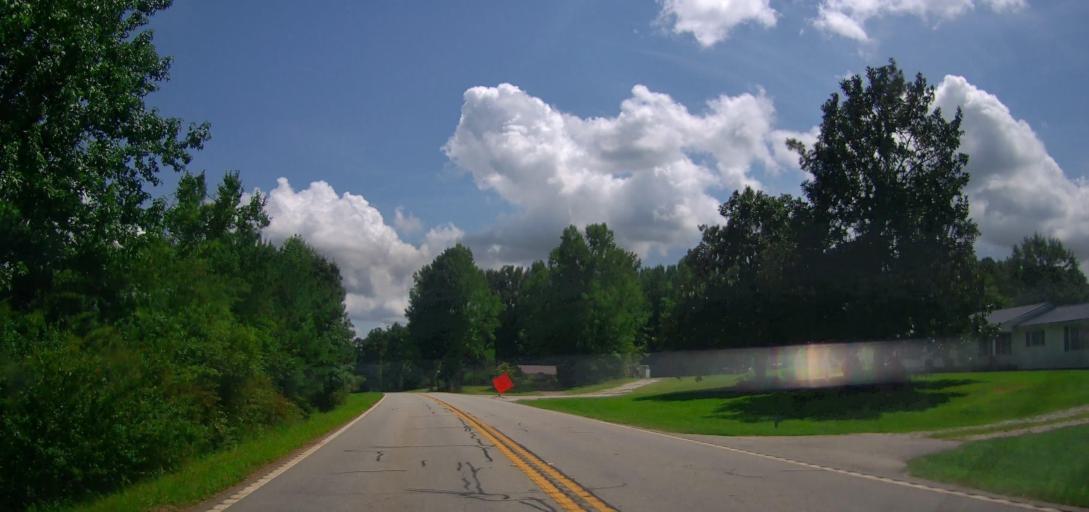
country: US
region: Georgia
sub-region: Carroll County
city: Bowdon
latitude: 33.3925
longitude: -85.2530
